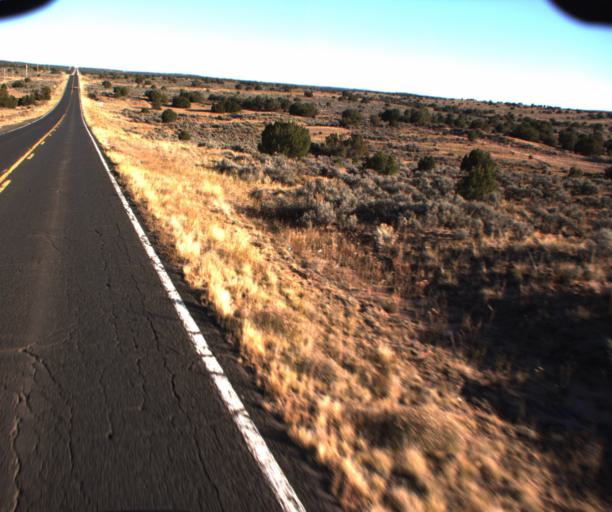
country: US
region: Arizona
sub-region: Apache County
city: Ganado
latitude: 35.5281
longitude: -109.5277
